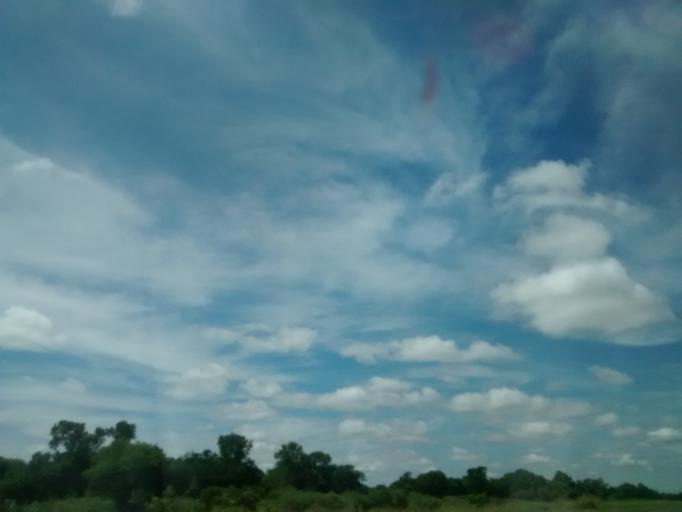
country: AR
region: Chaco
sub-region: Departamento de Quitilipi
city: Quitilipi
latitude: -26.7937
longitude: -60.1944
